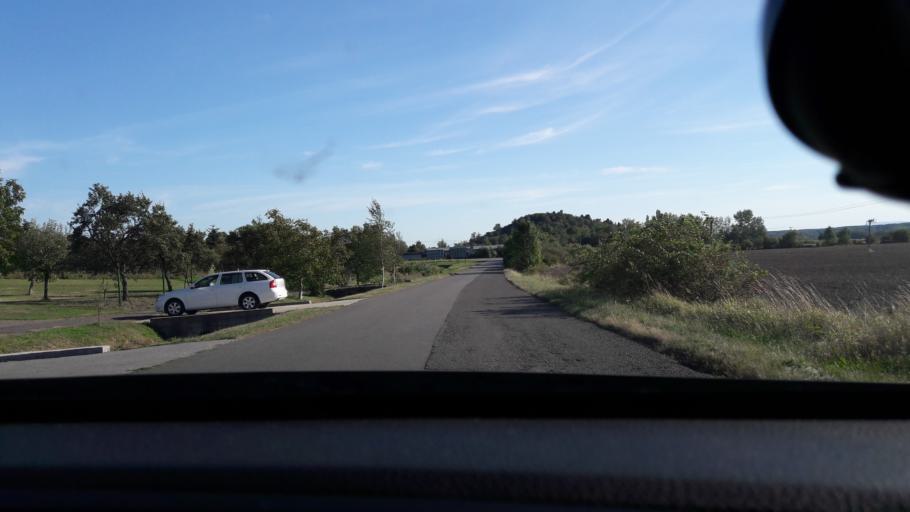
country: SK
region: Kosicky
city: Vinne
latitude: 48.8026
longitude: 21.9711
